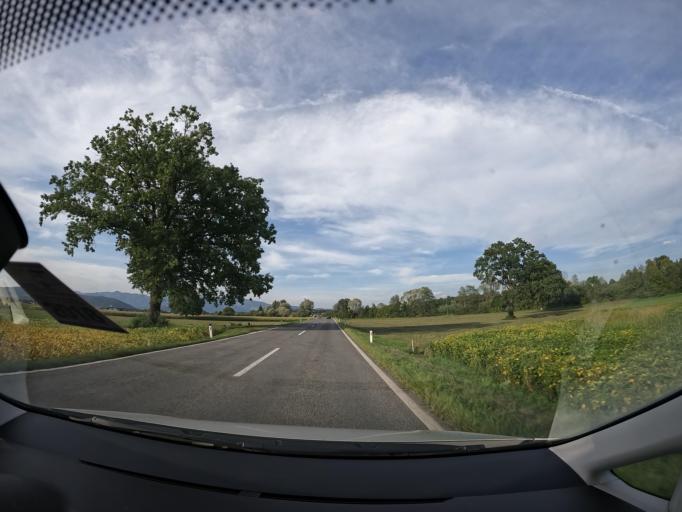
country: AT
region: Carinthia
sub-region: Politischer Bezirk Volkermarkt
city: Eberndorf
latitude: 46.6071
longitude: 14.6336
